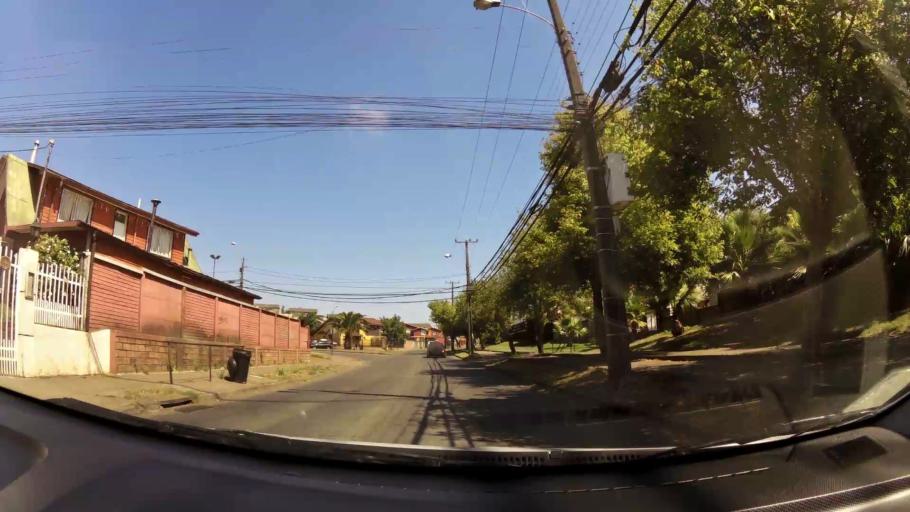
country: CL
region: Biobio
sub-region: Provincia de Concepcion
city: Concepcion
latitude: -36.7820
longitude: -73.0421
